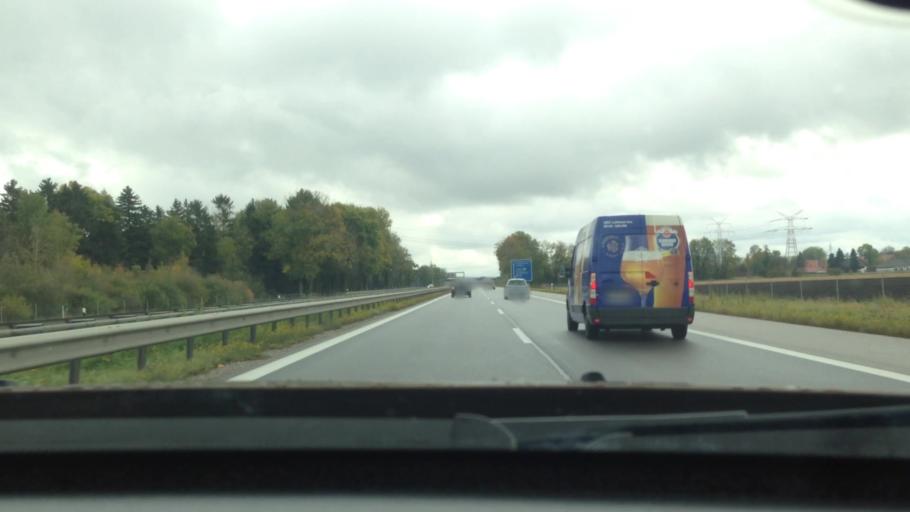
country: DE
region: Bavaria
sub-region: Upper Bavaria
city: Karlsfeld
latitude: 48.1896
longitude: 11.4200
